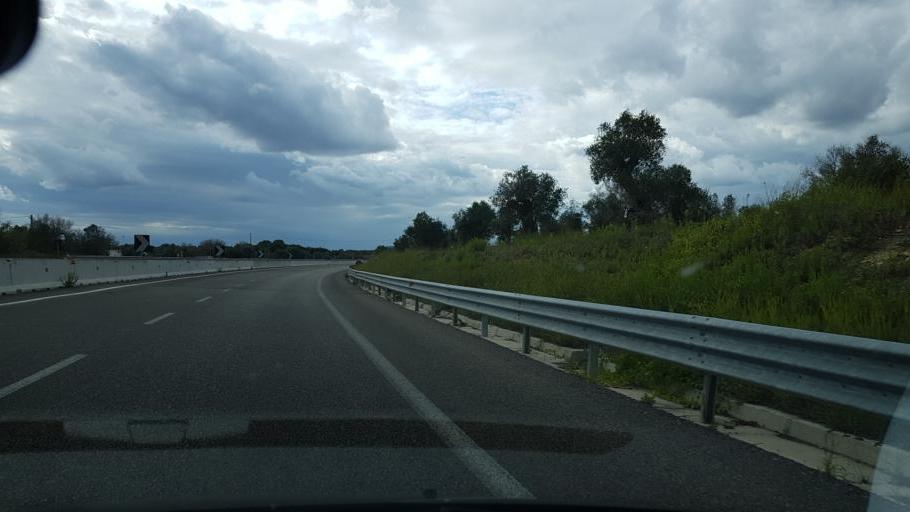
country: IT
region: Apulia
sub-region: Provincia di Lecce
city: Palmariggi
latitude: 40.1262
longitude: 18.3796
